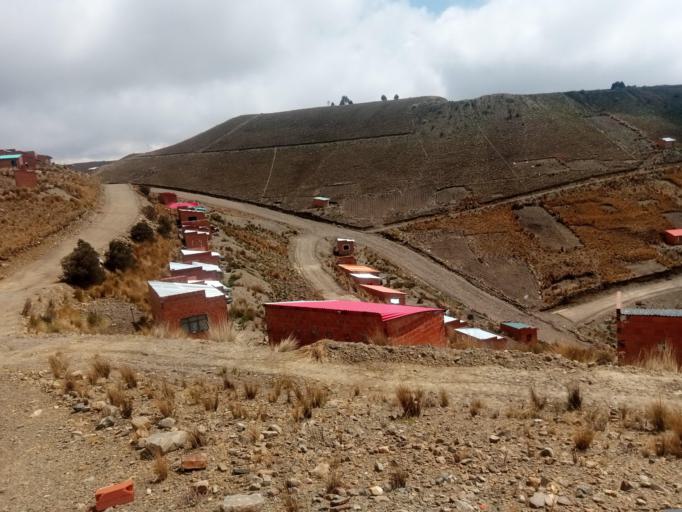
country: BO
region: La Paz
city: La Paz
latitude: -16.4629
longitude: -68.1376
